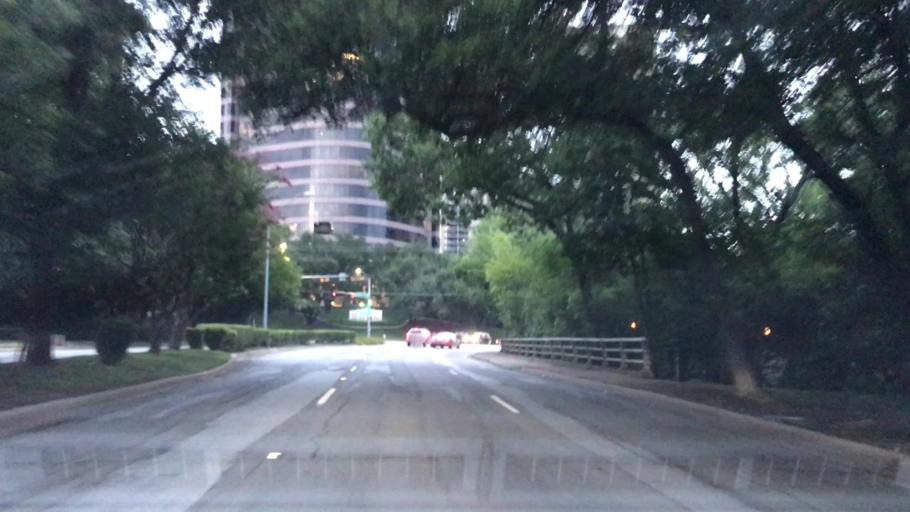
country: US
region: Texas
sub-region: Dallas County
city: Highland Park
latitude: 32.8123
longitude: -96.8012
